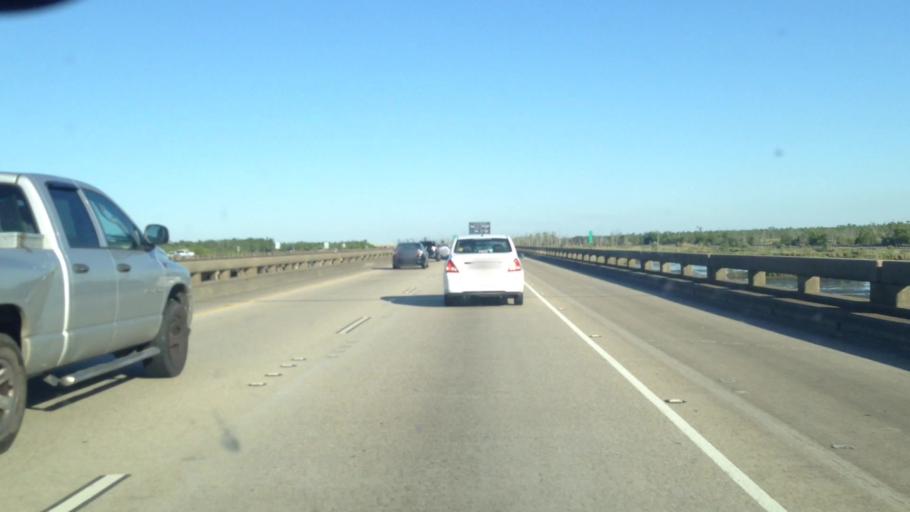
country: US
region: Louisiana
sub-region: Saint Charles Parish
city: Ama
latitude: 30.0149
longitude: -90.3122
